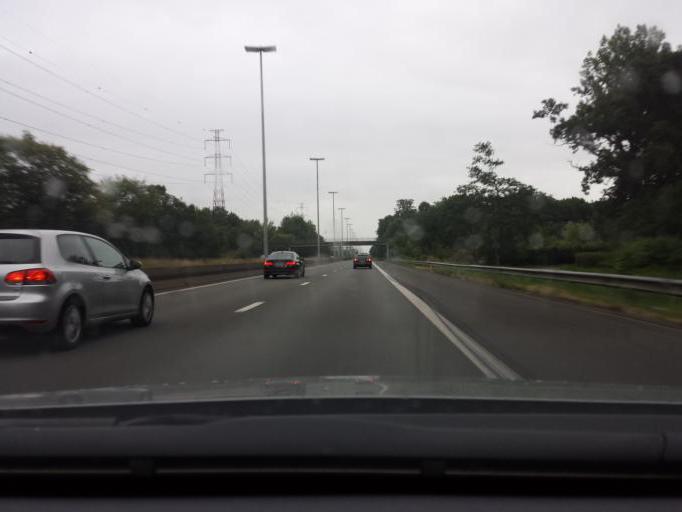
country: BE
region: Flanders
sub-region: Provincie Antwerpen
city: Ranst
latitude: 51.1972
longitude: 4.5986
